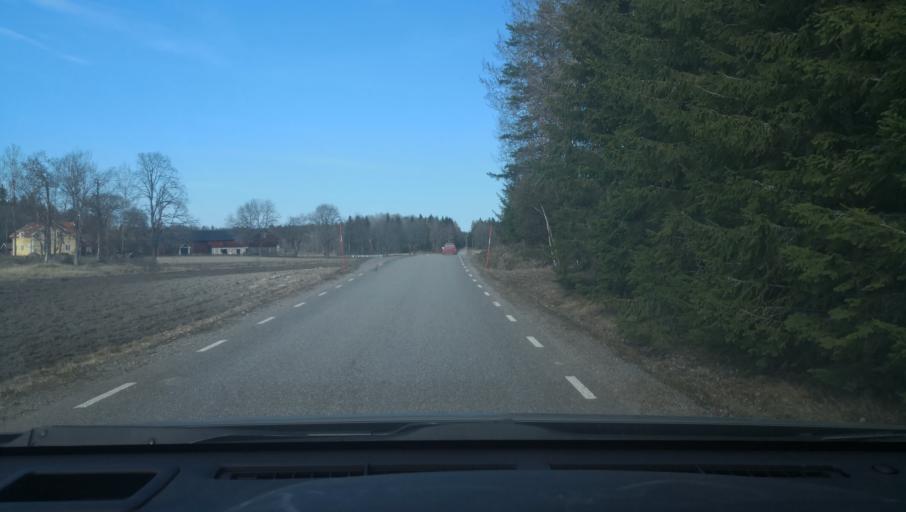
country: SE
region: Uppsala
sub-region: Heby Kommun
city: Heby
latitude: 59.9004
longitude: 16.8066
